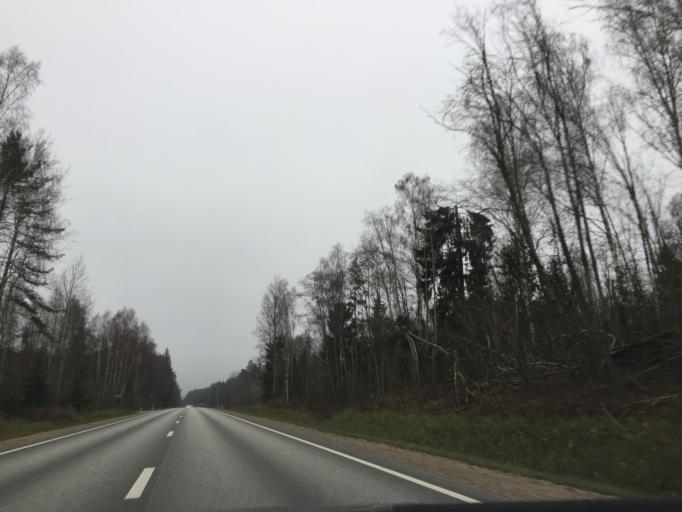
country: LV
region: Pargaujas
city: Stalbe
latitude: 57.3021
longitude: 24.9253
